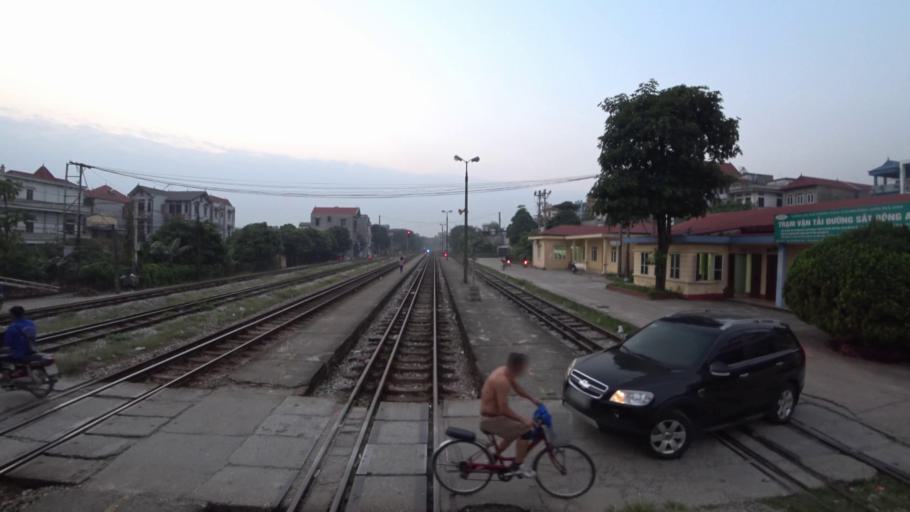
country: VN
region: Ha Noi
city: Soc Son
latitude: 21.2249
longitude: 105.8608
